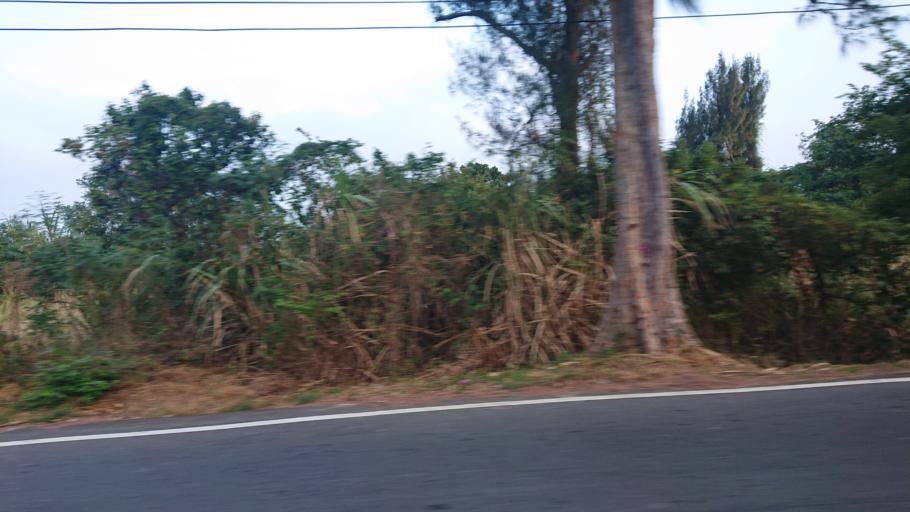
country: CN
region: Fujian
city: Dadeng
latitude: 24.4852
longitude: 118.4390
